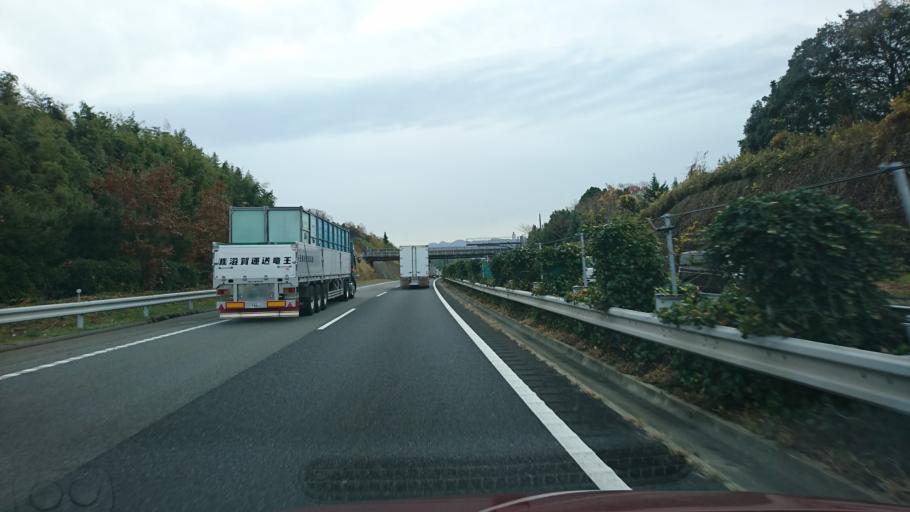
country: JP
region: Hyogo
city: Sandacho
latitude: 34.8302
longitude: 135.1678
